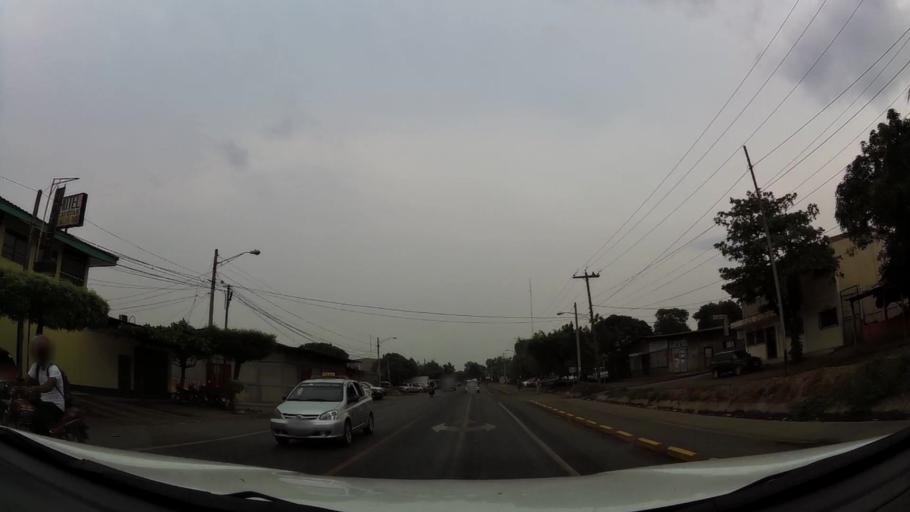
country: NI
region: Leon
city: Leon
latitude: 12.4487
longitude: -86.8635
